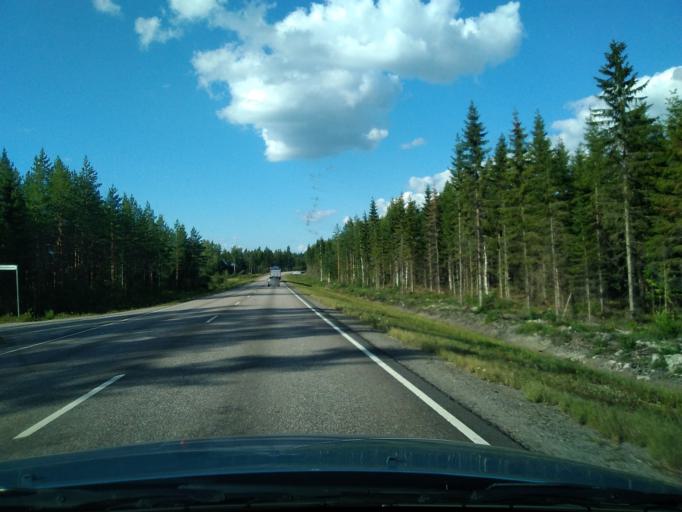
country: FI
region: Central Finland
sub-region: Keuruu
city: Keuruu
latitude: 62.1547
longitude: 24.7504
